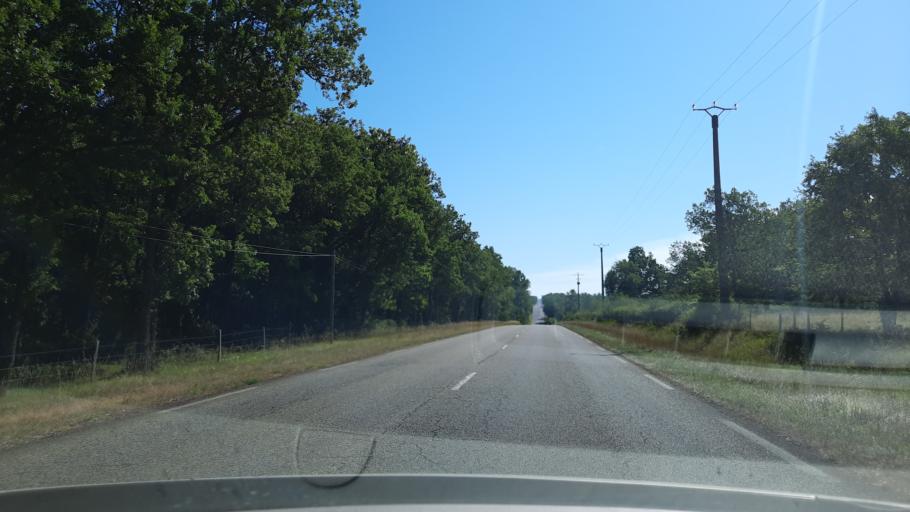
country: FR
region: Midi-Pyrenees
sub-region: Departement du Tarn-et-Garonne
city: Septfonds
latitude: 44.1835
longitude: 1.6442
